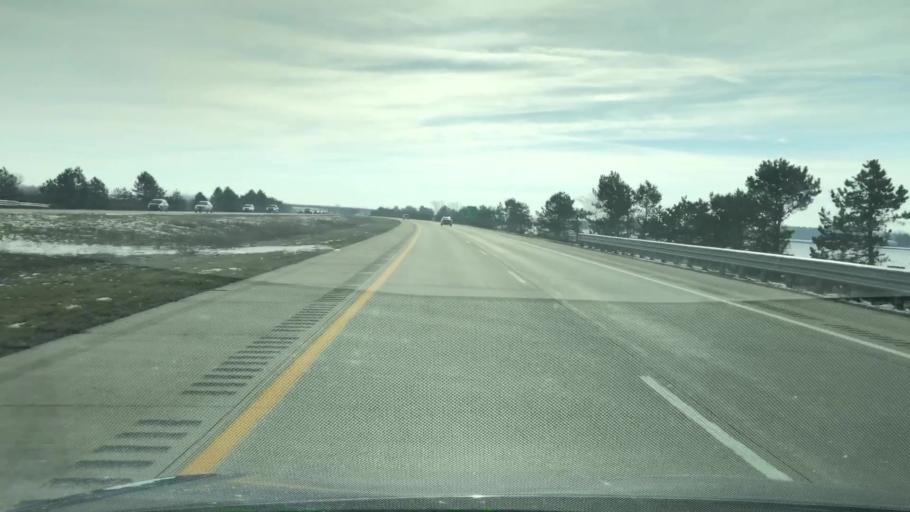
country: US
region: Michigan
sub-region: Bay County
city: Pinconning
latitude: 43.8759
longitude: -84.0224
